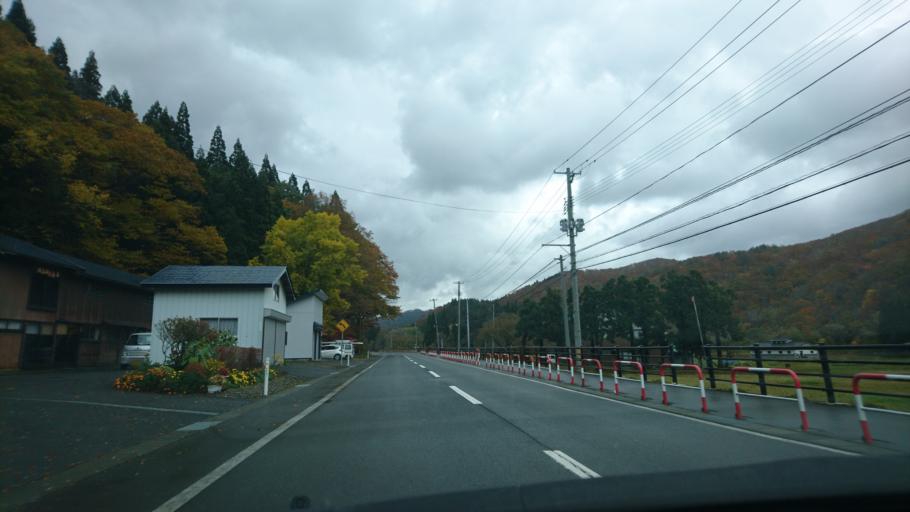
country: JP
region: Iwate
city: Shizukuishi
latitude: 39.5079
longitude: 140.8269
